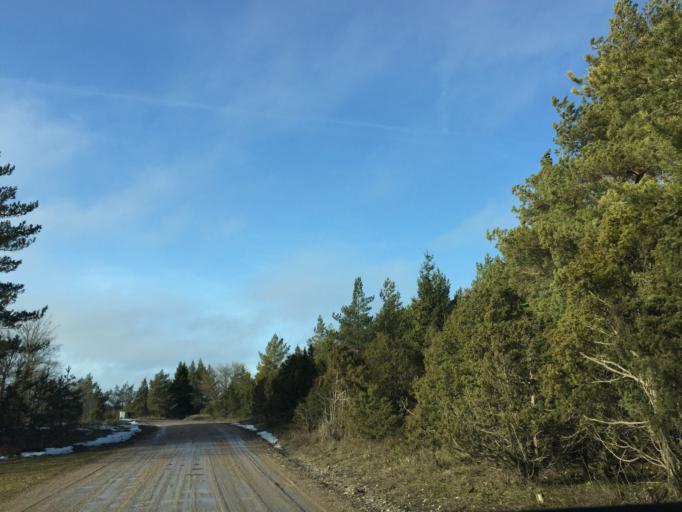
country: EE
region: Saare
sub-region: Kuressaare linn
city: Kuressaare
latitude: 58.4708
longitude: 21.9638
